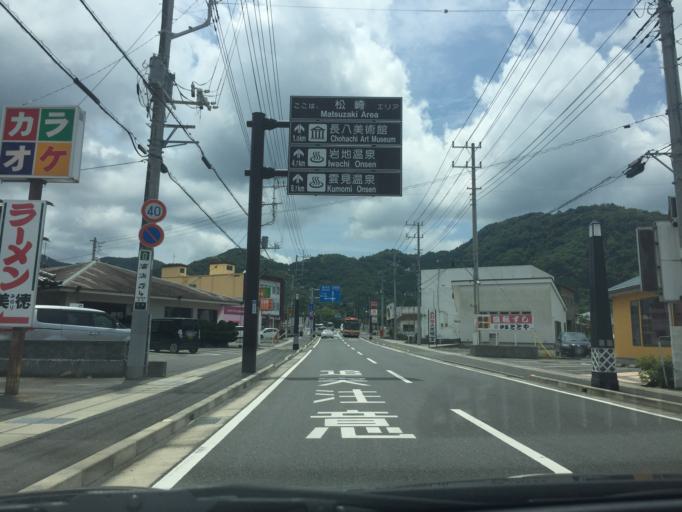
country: JP
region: Shizuoka
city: Shimoda
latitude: 34.7552
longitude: 138.7805
